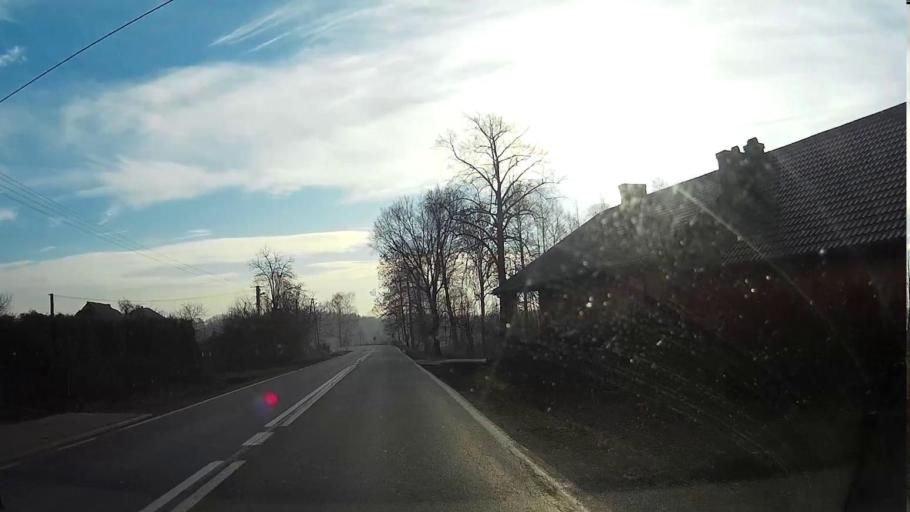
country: PL
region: Lesser Poland Voivodeship
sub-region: Powiat chrzanowski
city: Brodla
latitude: 50.0413
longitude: 19.5942
